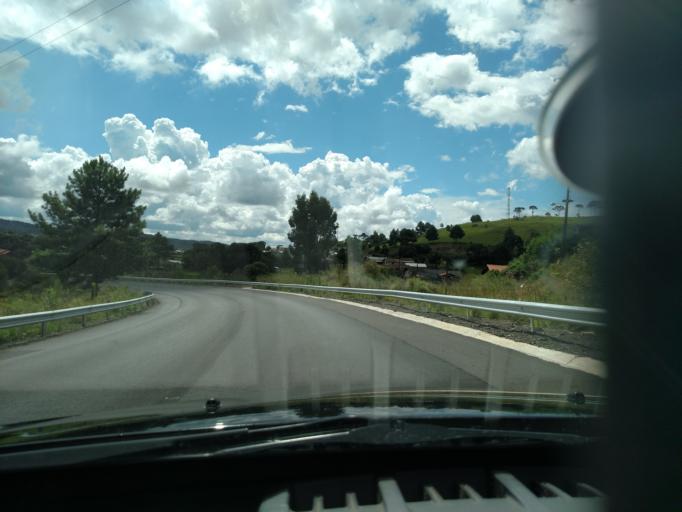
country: BR
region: Santa Catarina
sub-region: Lages
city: Lages
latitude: -27.9280
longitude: -50.0986
